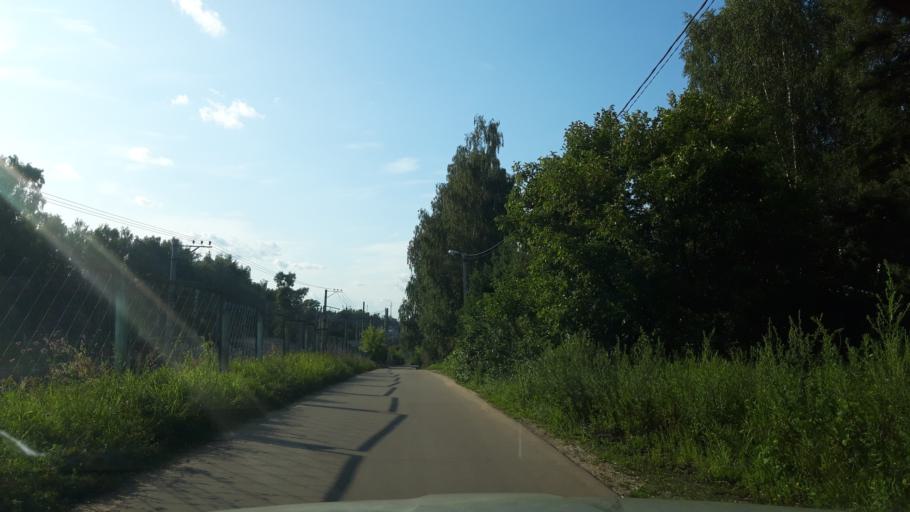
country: RU
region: Moskovskaya
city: Povarovo
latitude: 56.0638
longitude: 37.0774
